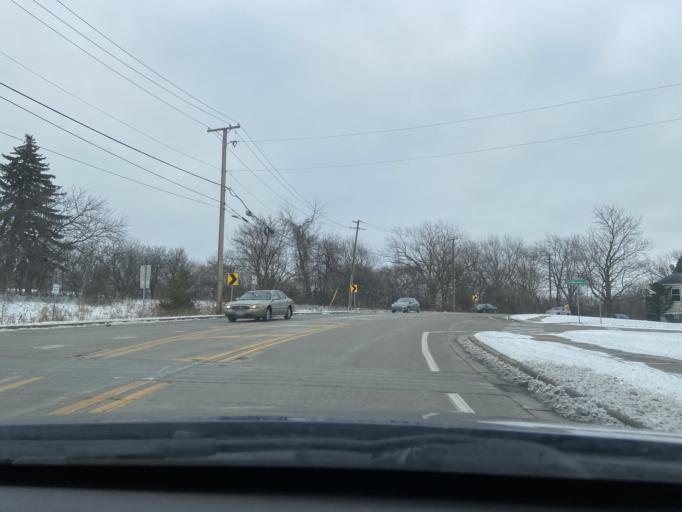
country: US
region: Illinois
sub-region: Lake County
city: Venetian Village
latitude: 42.3783
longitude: -88.0644
